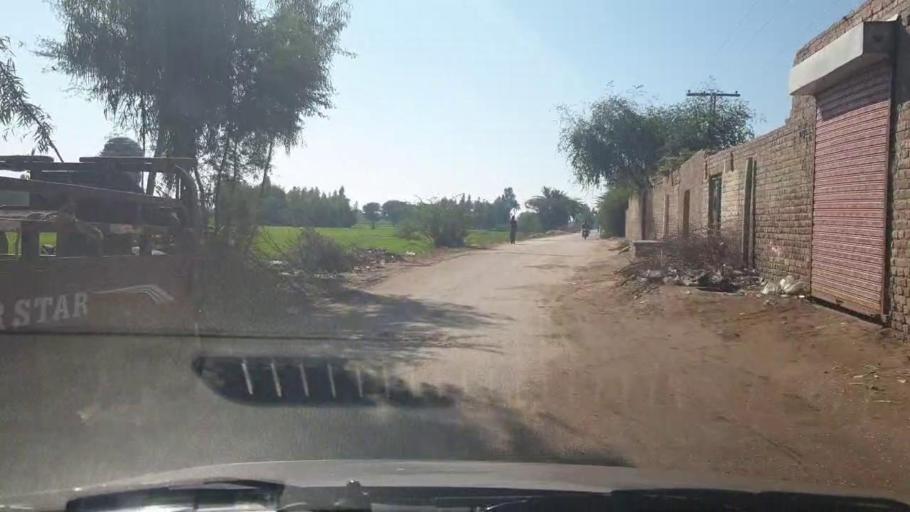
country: PK
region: Sindh
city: Bozdar
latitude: 27.1054
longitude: 68.6327
